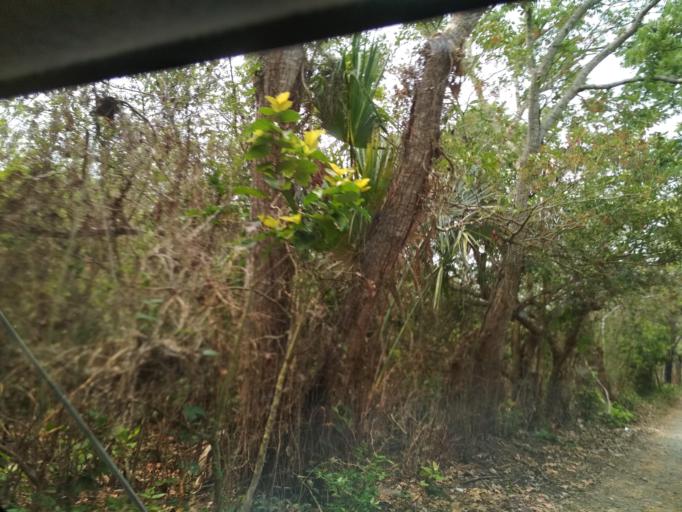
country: MX
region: Veracruz
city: Paso del Toro
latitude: 19.0252
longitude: -96.1409
